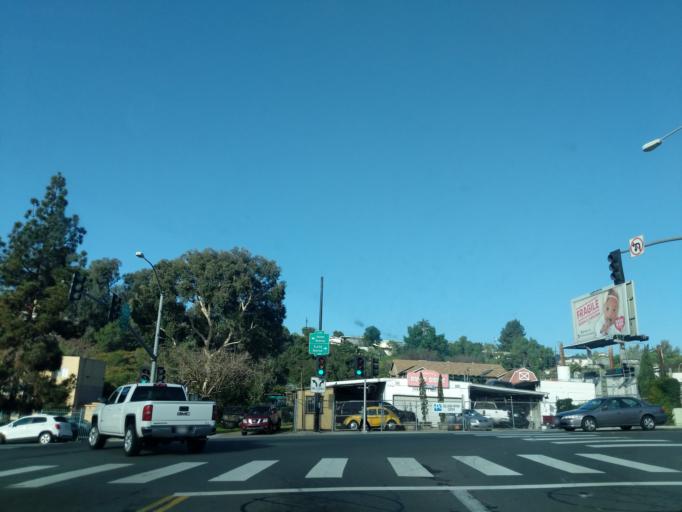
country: US
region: California
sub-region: San Diego County
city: National City
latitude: 32.7372
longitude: -117.0920
